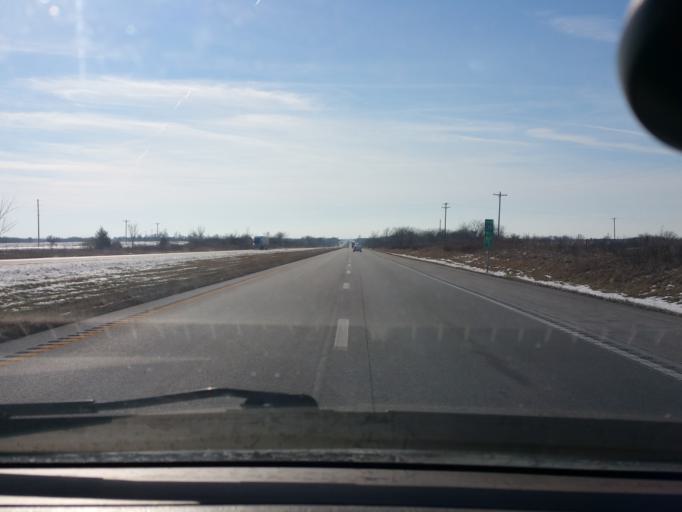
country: US
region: Missouri
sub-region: Clinton County
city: Cameron
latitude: 39.8336
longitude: -94.1858
